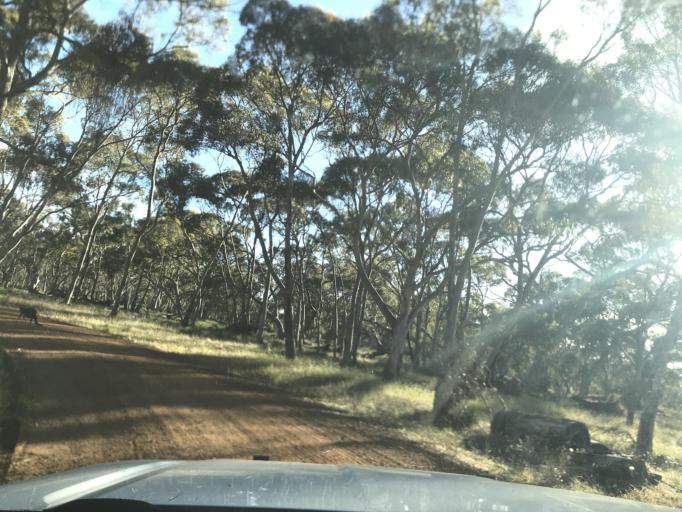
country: AU
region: South Australia
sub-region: Wattle Range
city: Penola
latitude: -37.1192
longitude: 141.4453
